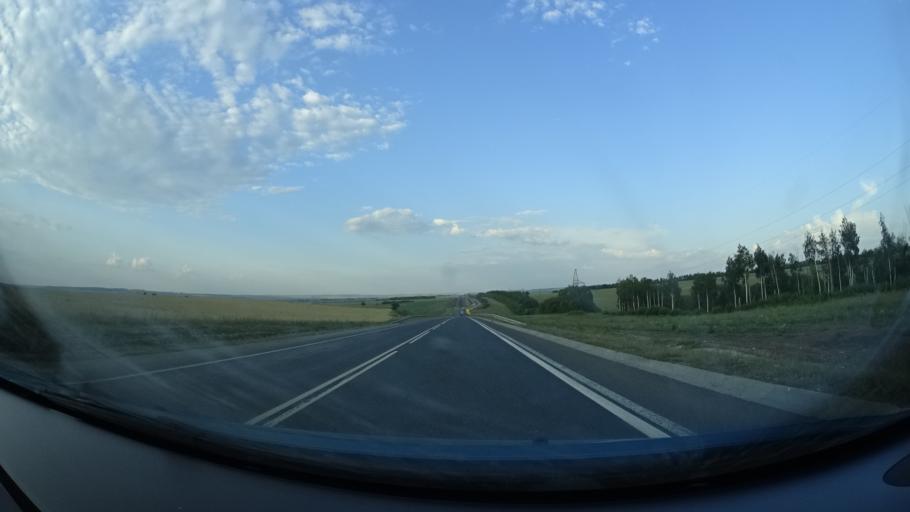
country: RU
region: Samara
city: Kamyshla
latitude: 54.0333
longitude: 51.9299
